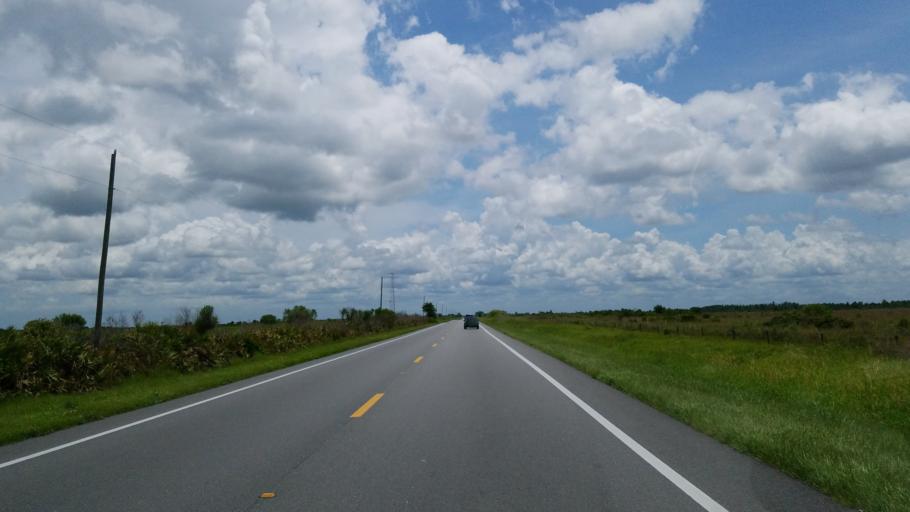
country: US
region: Florida
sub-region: Indian River County
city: Fellsmere
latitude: 27.7407
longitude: -81.0424
